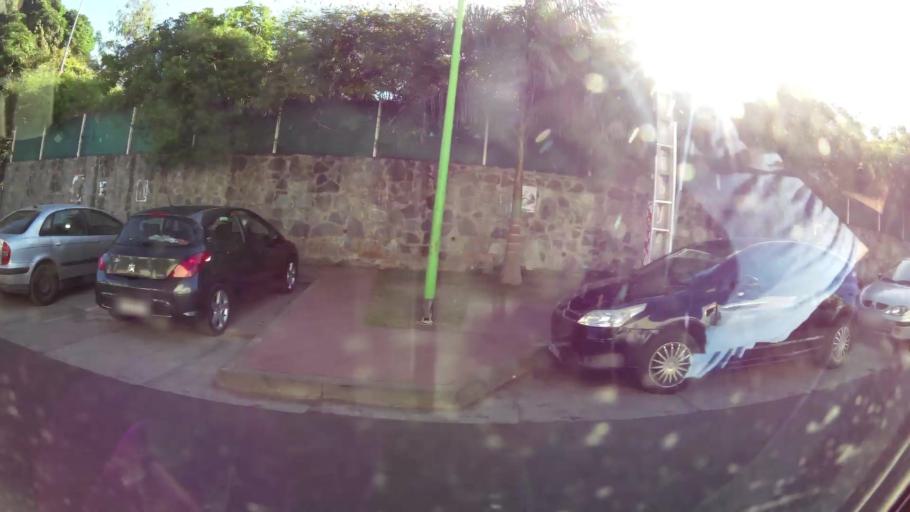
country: YT
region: Pamandzi
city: Pamandzi
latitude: -12.7966
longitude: 45.2742
